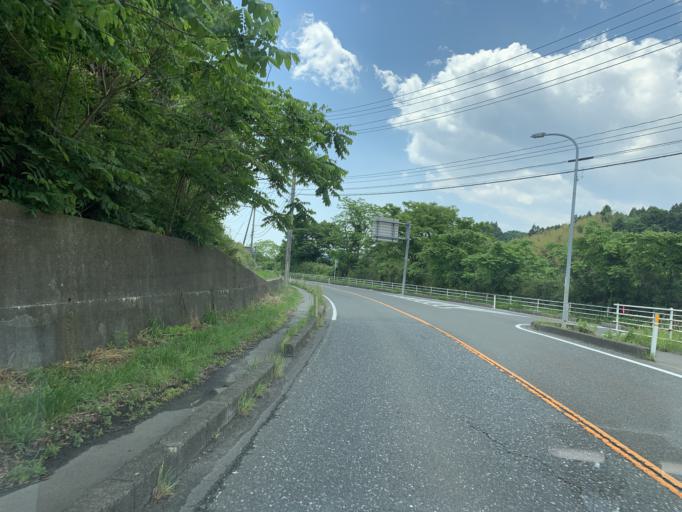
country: JP
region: Miyagi
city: Matsushima
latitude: 38.4041
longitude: 141.0665
